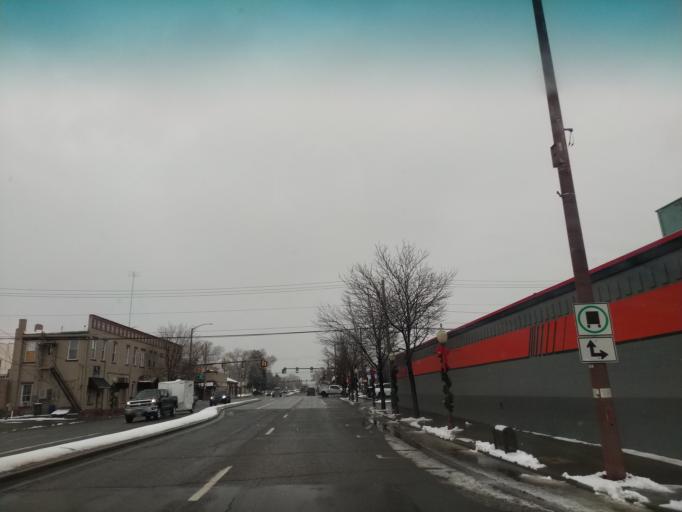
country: US
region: Colorado
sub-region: Montrose County
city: Montrose
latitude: 38.4795
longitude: -107.8788
